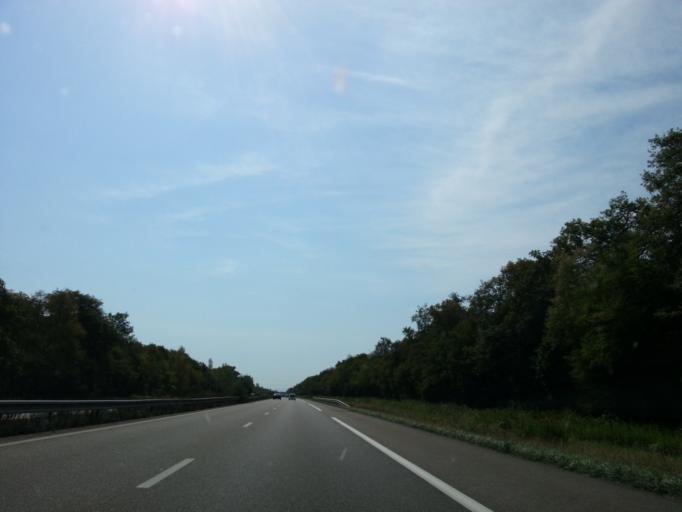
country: FR
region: Alsace
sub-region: Departement du Haut-Rhin
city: Sierentz
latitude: 47.6853
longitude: 7.4541
